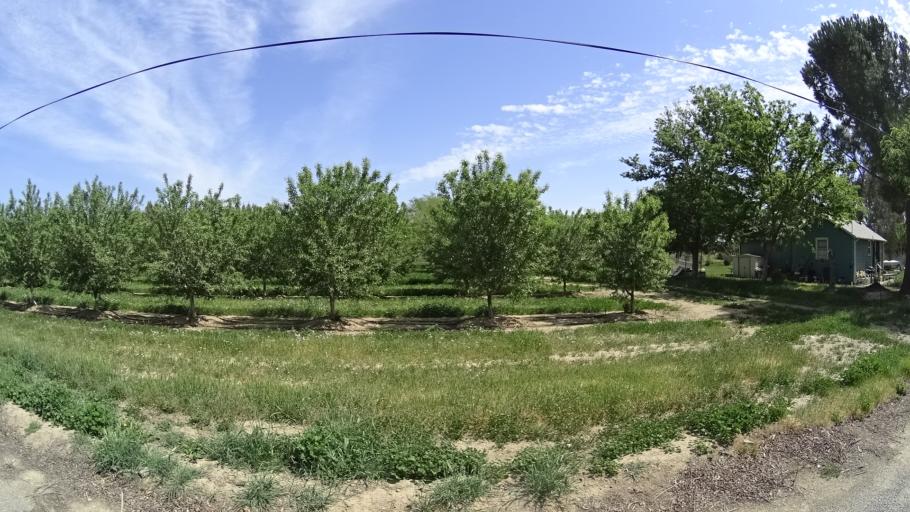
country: US
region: California
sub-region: Glenn County
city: Willows
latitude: 39.5831
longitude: -122.1969
